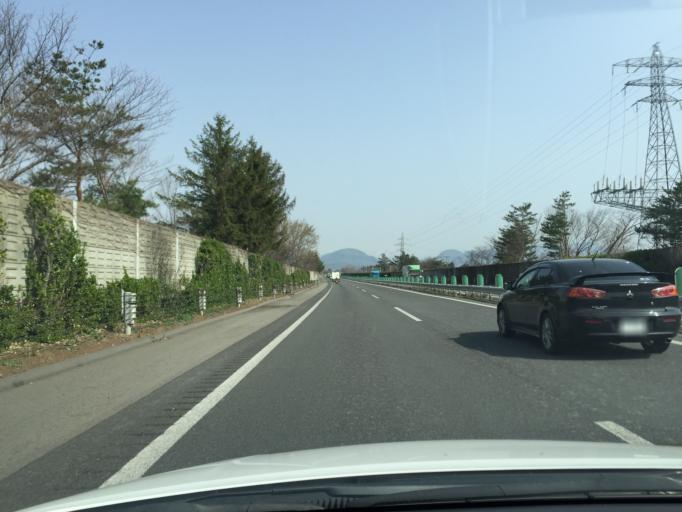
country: JP
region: Fukushima
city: Fukushima-shi
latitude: 37.7714
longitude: 140.4128
